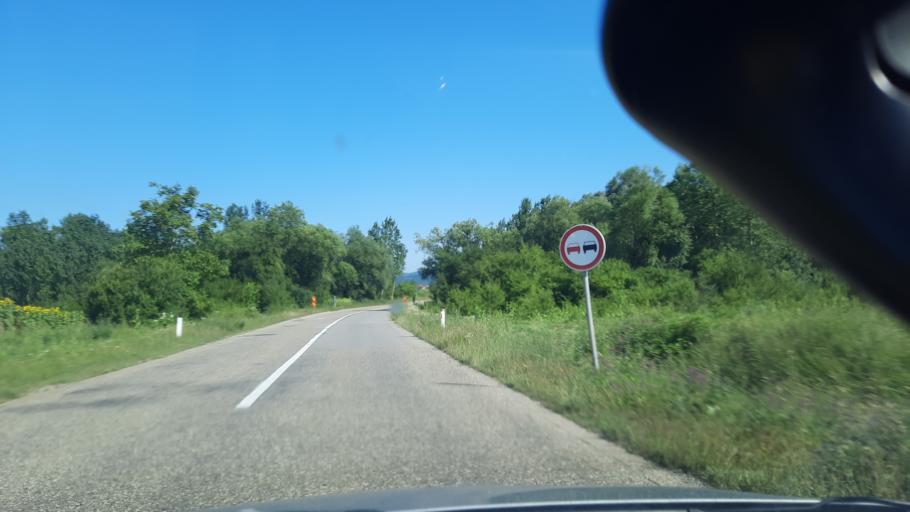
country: RS
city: Turija
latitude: 44.5632
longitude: 21.5307
